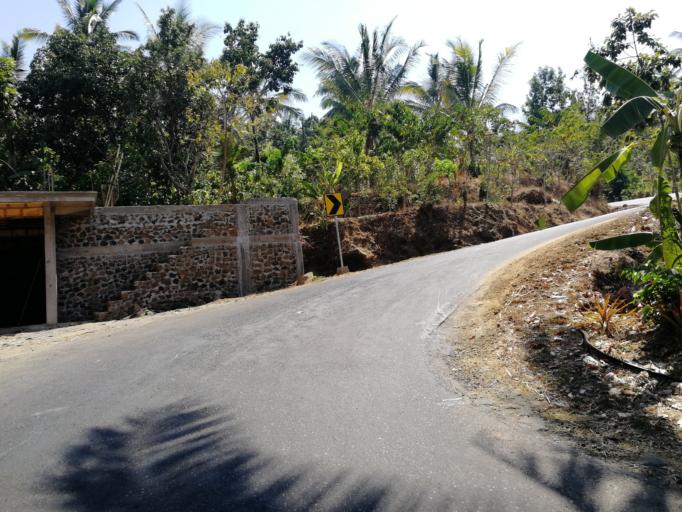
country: ID
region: Bali
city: Banjar Kedisan
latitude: -8.1403
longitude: 115.3160
